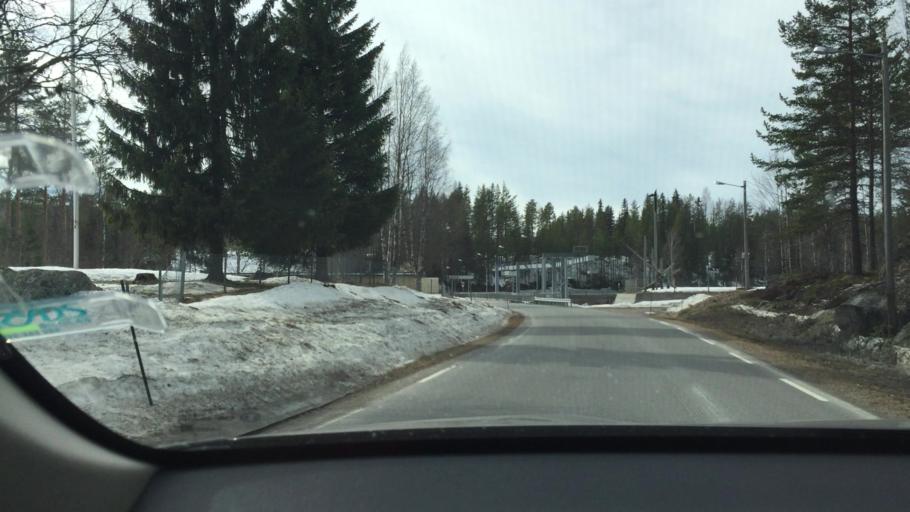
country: NO
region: Hedmark
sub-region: Trysil
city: Innbygda
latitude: 61.0657
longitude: 12.5838
